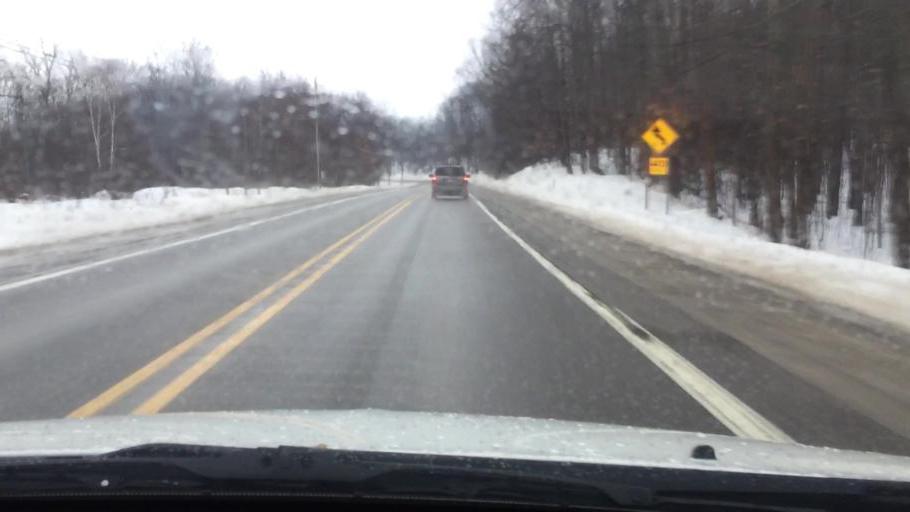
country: US
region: Michigan
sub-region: Charlevoix County
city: East Jordan
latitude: 45.2224
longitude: -85.1766
